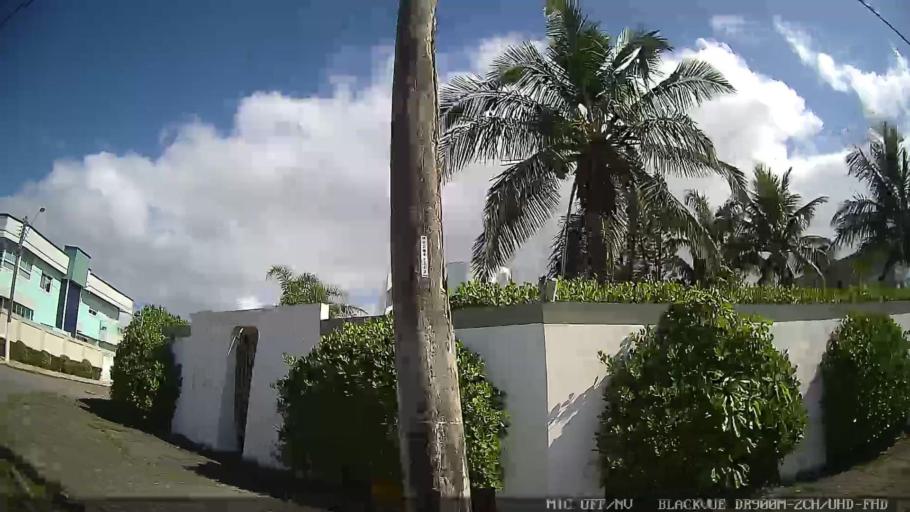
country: BR
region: Sao Paulo
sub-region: Peruibe
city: Peruibe
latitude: -24.2974
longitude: -46.9651
